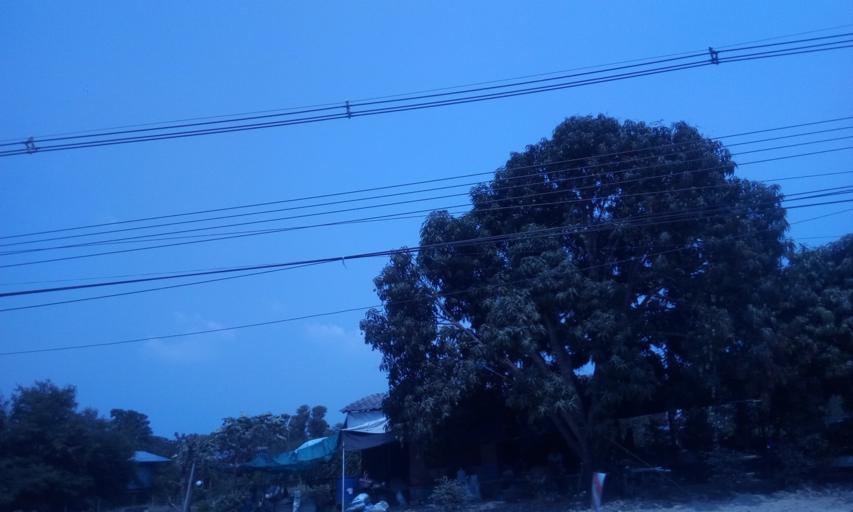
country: TH
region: Chachoengsao
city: Ban Pho
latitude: 13.5658
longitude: 101.1315
